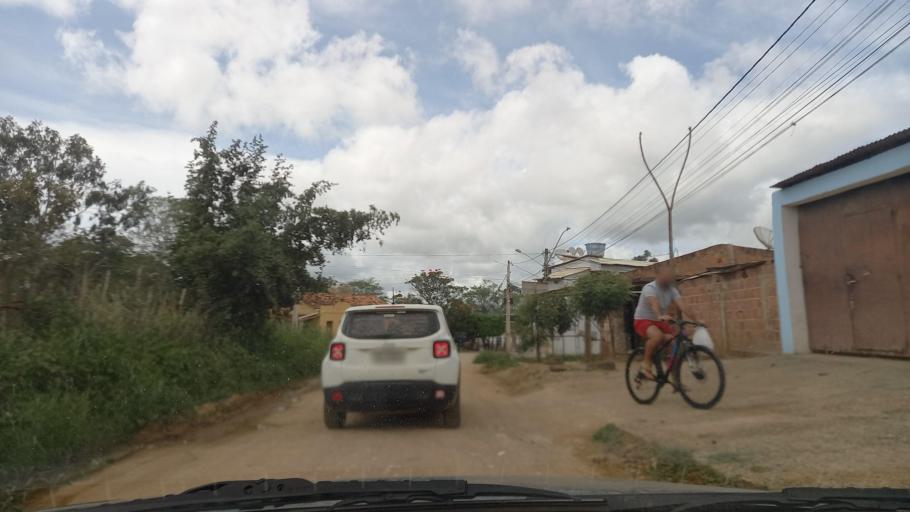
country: BR
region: Pernambuco
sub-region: Gravata
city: Gravata
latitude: -8.1878
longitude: -35.5794
